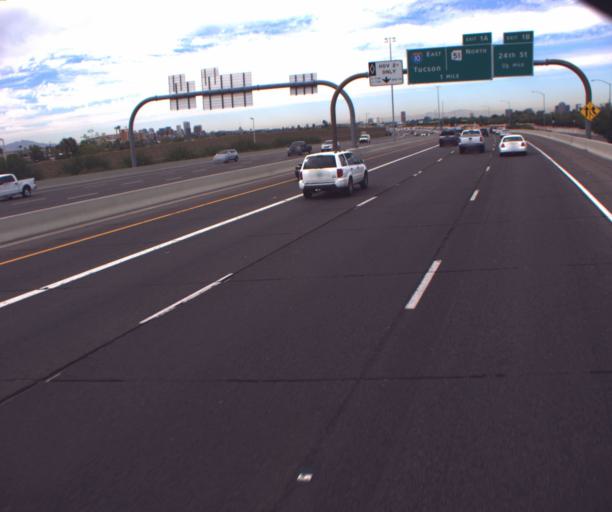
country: US
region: Arizona
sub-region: Maricopa County
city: Phoenix
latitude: 33.4611
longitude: -112.0137
